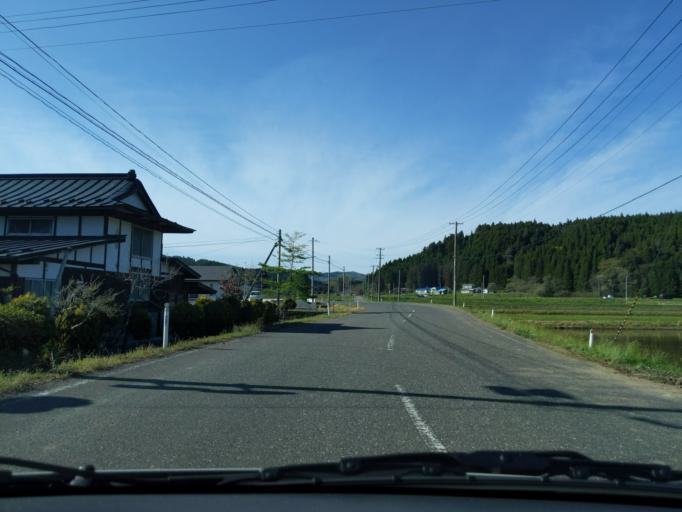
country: JP
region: Iwate
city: Ichinoseki
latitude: 38.8397
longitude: 140.9090
